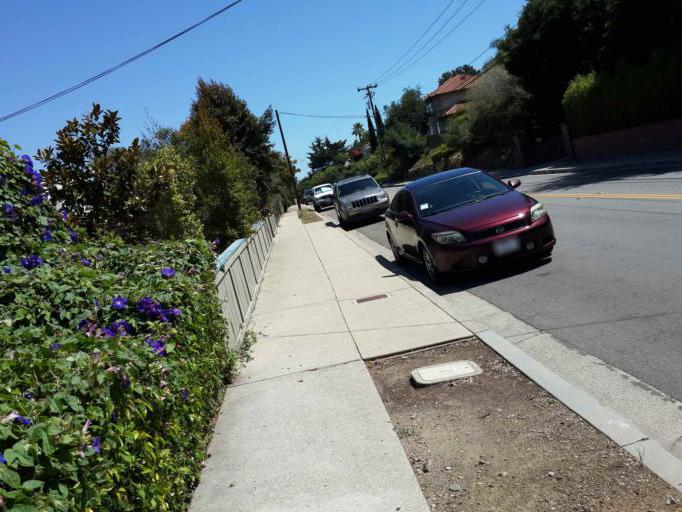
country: US
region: California
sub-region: San Luis Obispo County
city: San Luis Obispo
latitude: 35.2880
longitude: -120.6712
